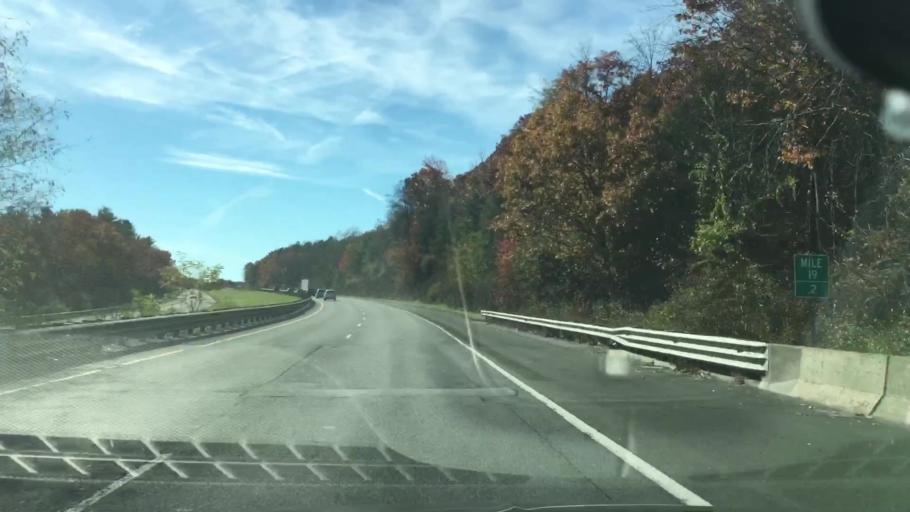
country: US
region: Massachusetts
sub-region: Hampshire County
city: South Hadley
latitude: 42.2659
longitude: -72.6126
